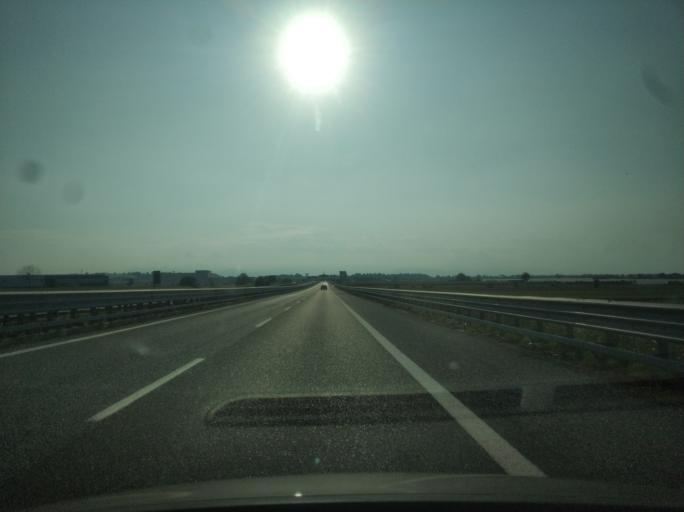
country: IT
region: Piedmont
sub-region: Provincia di Cuneo
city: Cervere
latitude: 44.6643
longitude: 7.7967
